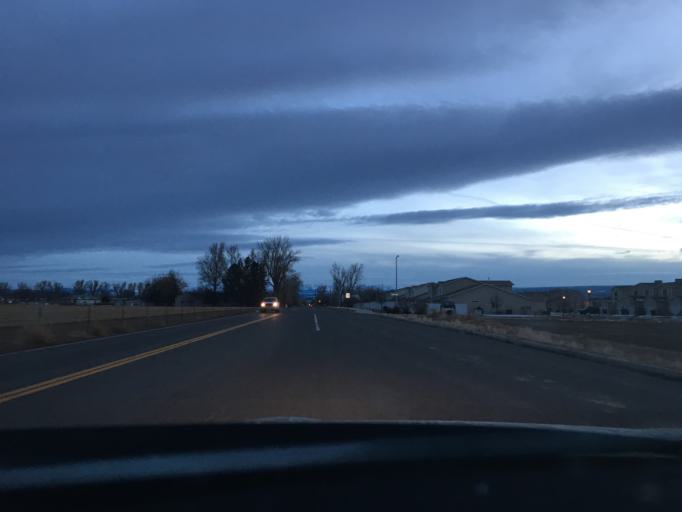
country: US
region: Colorado
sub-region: Montrose County
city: Montrose
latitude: 38.4883
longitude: -107.8387
